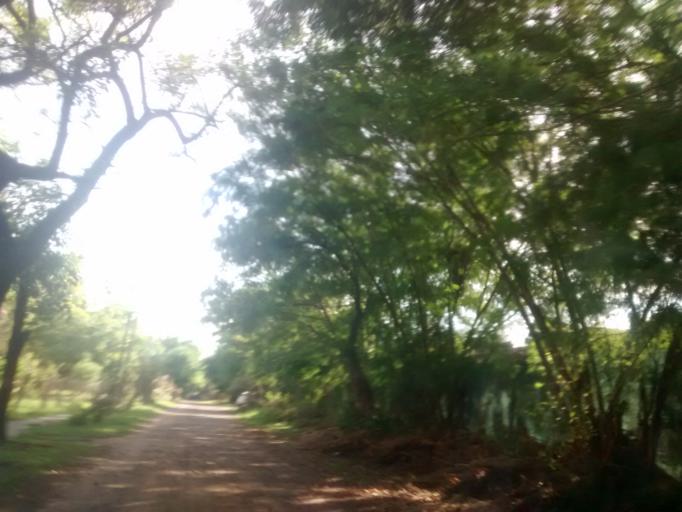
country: AR
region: Chaco
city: Puerto Tirol
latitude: -27.3704
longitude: -59.0876
